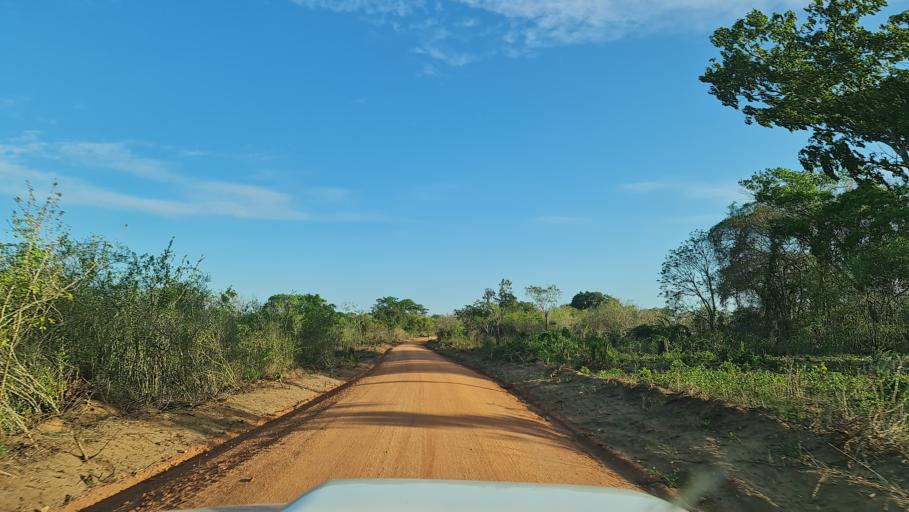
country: MZ
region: Nampula
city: Nacala
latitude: -14.6875
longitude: 40.3137
